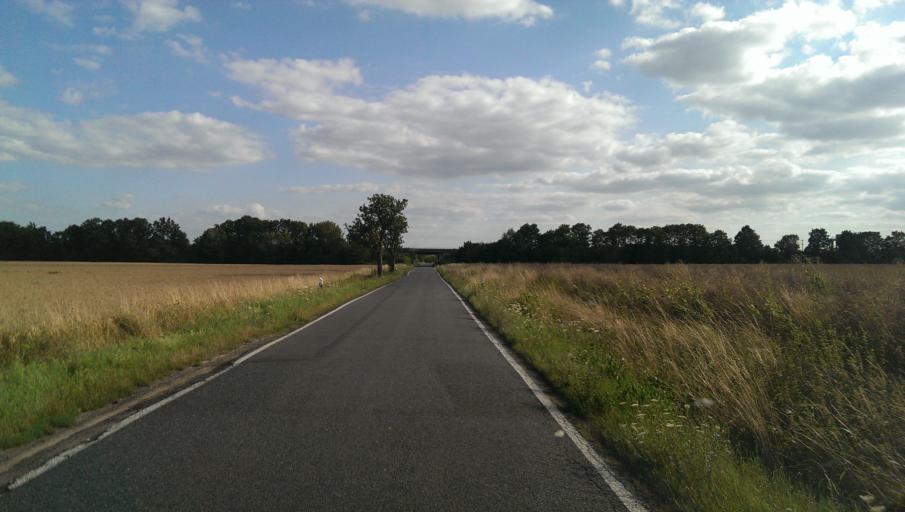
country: DE
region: Saxony
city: Rackwitz
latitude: 51.4106
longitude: 12.3769
